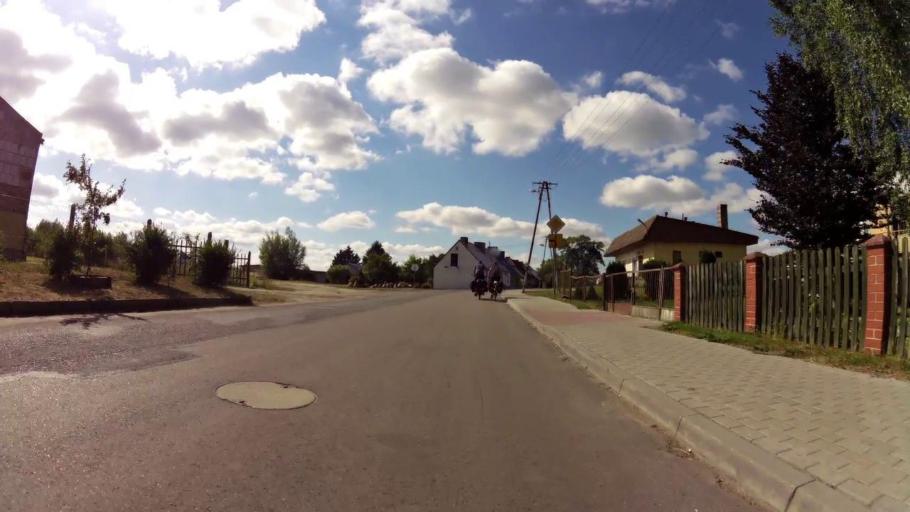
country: PL
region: West Pomeranian Voivodeship
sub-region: Powiat lobeski
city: Lobez
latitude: 53.6436
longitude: 15.6708
